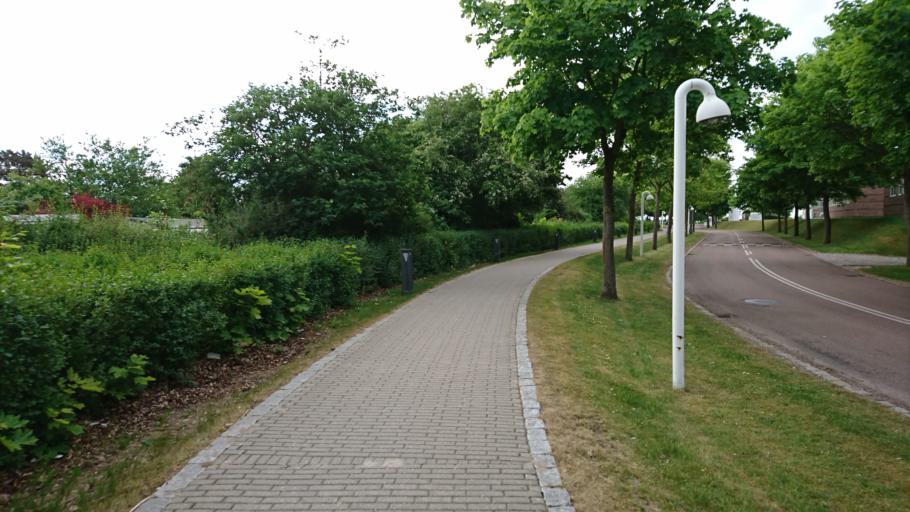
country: DK
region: Capital Region
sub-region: Ballerup Kommune
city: Ballerup
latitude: 55.7390
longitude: 12.4000
